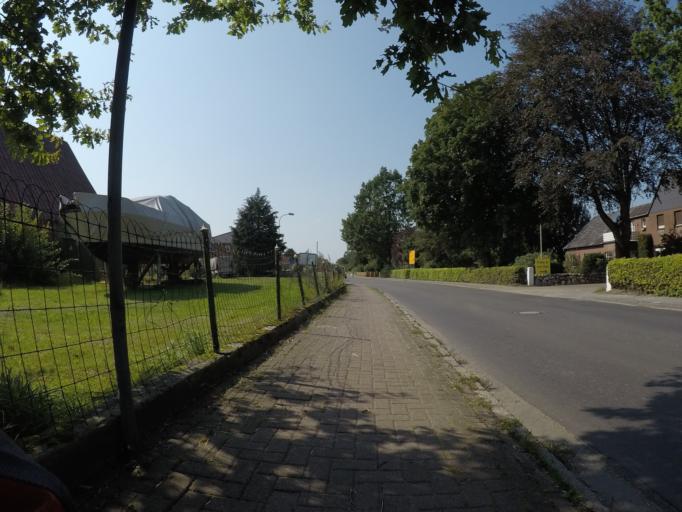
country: DE
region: Schleswig-Holstein
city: Stuvenborn
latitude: 53.8514
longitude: 10.1220
